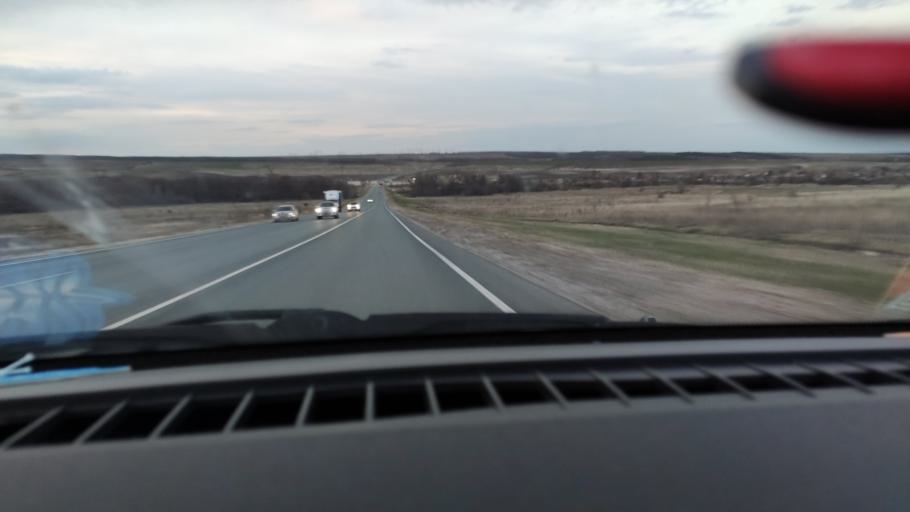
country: RU
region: Saratov
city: Sinodskoye
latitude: 51.9198
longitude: 46.5599
